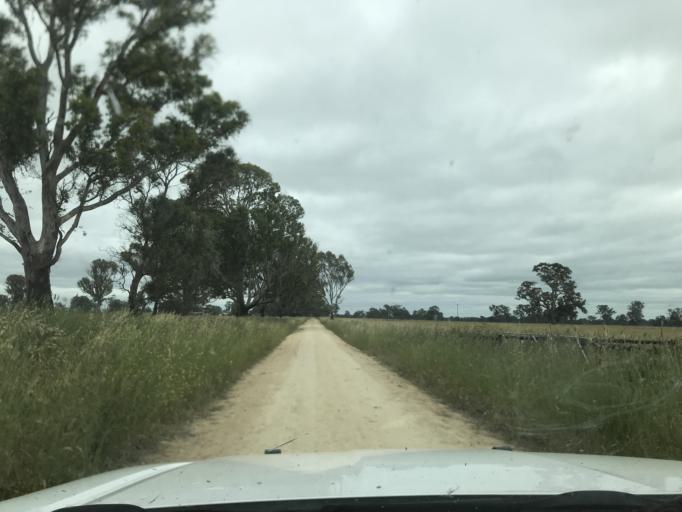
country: AU
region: South Australia
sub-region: Wattle Range
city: Penola
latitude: -37.1803
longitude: 141.0726
